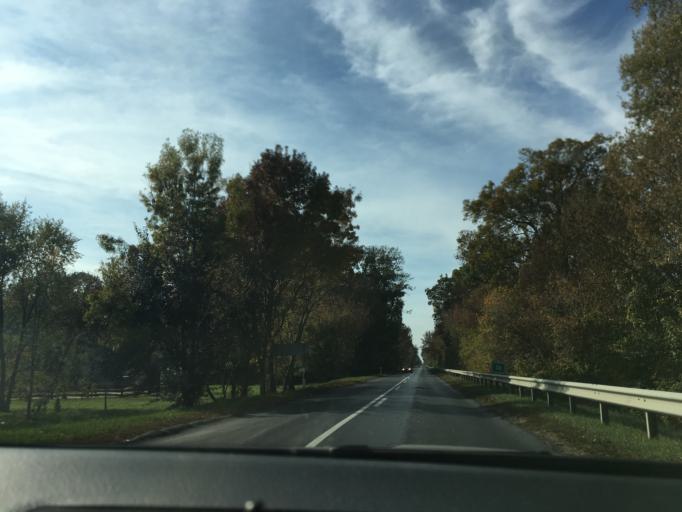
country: HU
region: Hajdu-Bihar
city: Vamospercs
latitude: 47.5291
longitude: 21.8241
